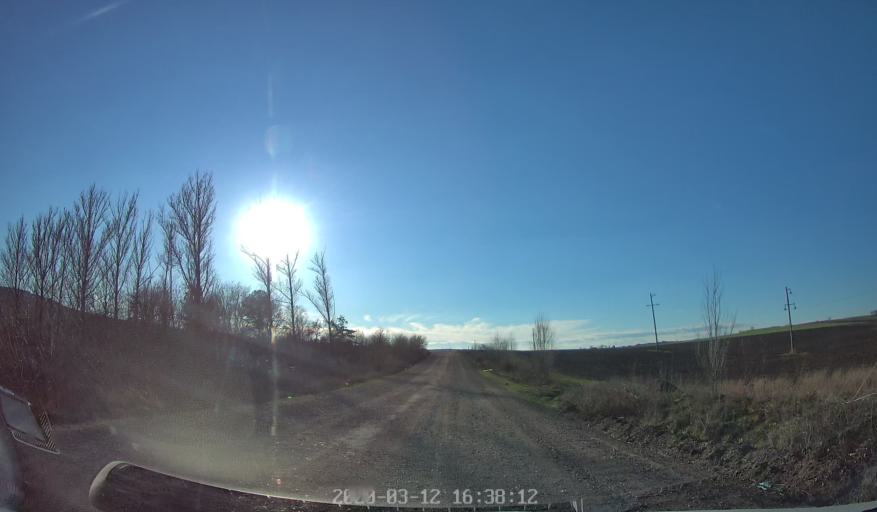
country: MD
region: Anenii Noi
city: Anenii Noi
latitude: 46.8155
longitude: 29.1816
